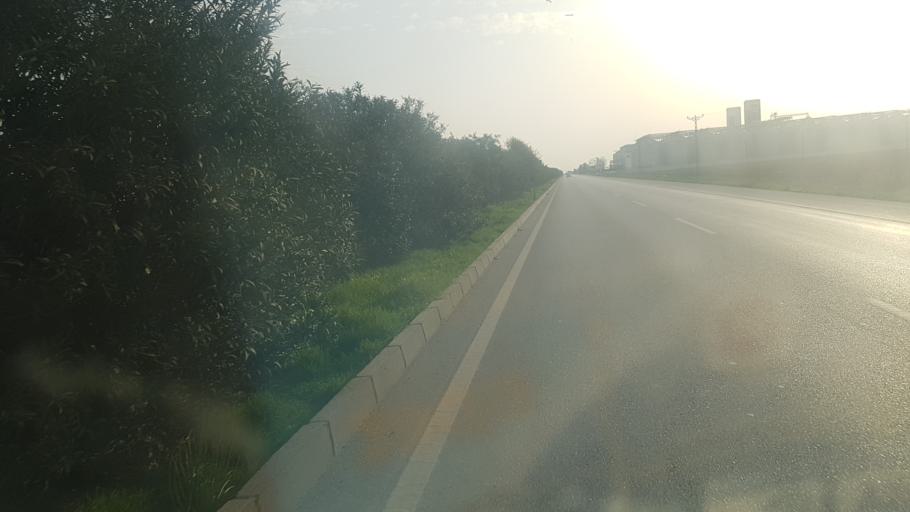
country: TR
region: Adana
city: Ceyhan
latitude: 37.0566
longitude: 35.8798
